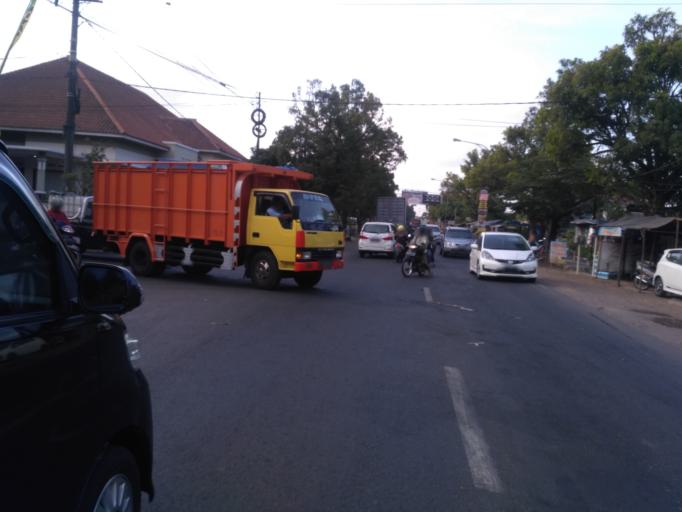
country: ID
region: East Java
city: Kebonsari
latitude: -8.0276
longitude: 112.6159
